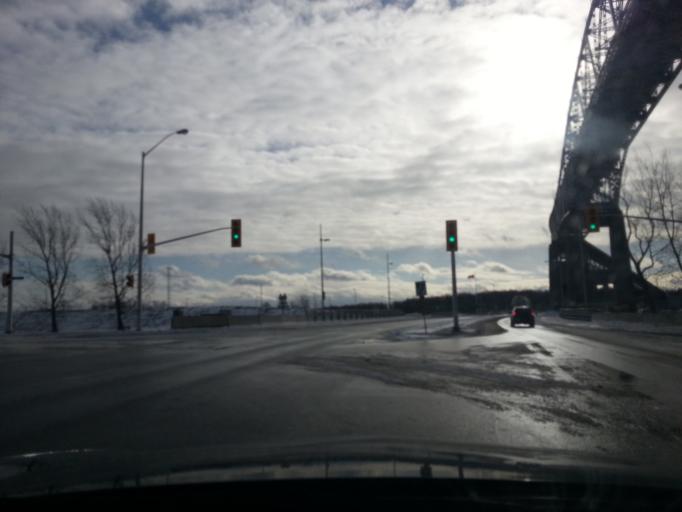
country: CA
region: Ontario
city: Cornwall
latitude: 45.0121
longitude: -74.7391
